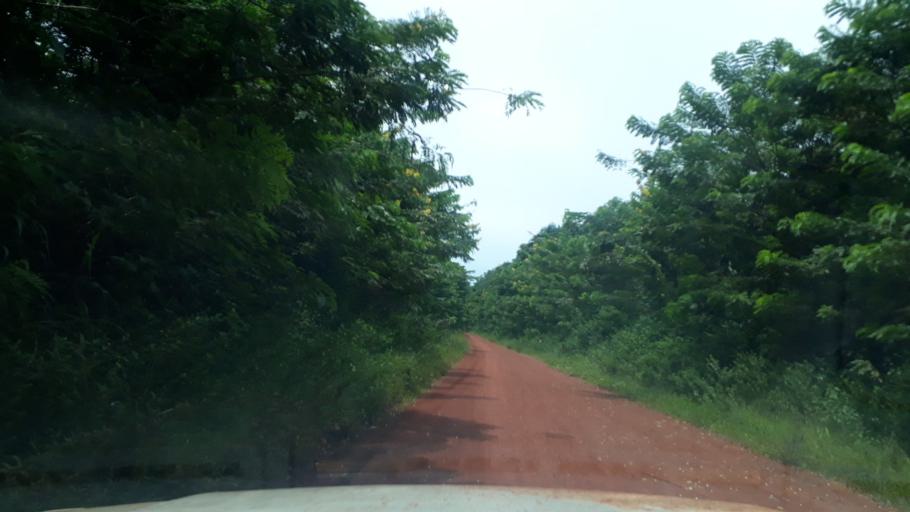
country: CD
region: Eastern Province
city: Aketi
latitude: 2.9320
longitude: 24.0920
